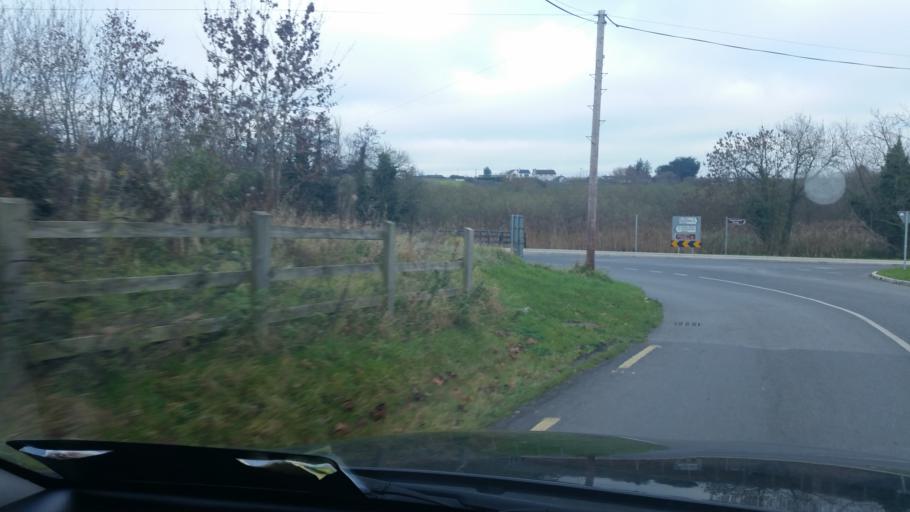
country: IE
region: Leinster
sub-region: Lu
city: Tullyallen
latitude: 53.7203
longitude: -6.4089
